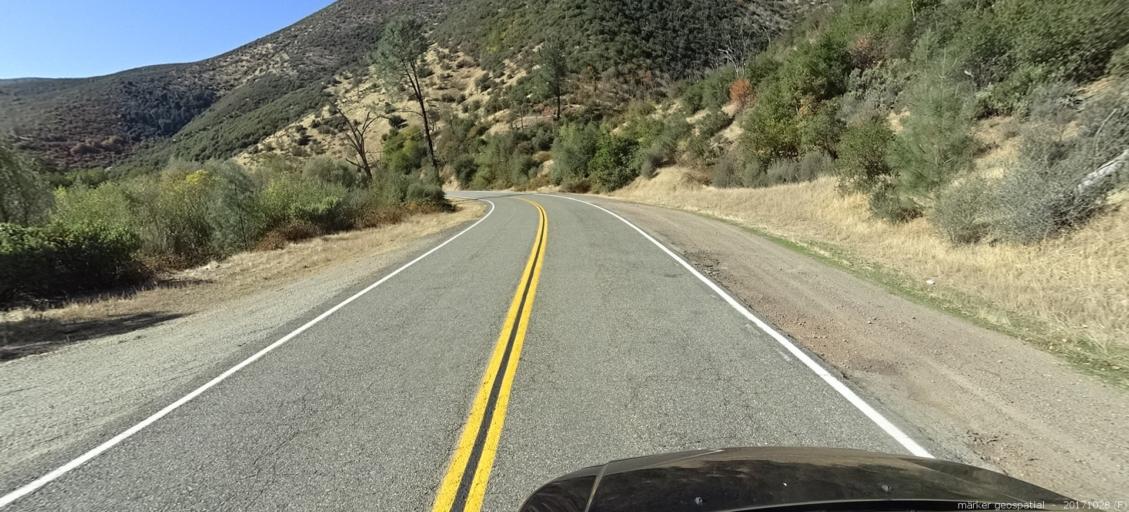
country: US
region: California
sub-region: Trinity County
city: Lewiston
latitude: 40.7174
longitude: -122.6348
